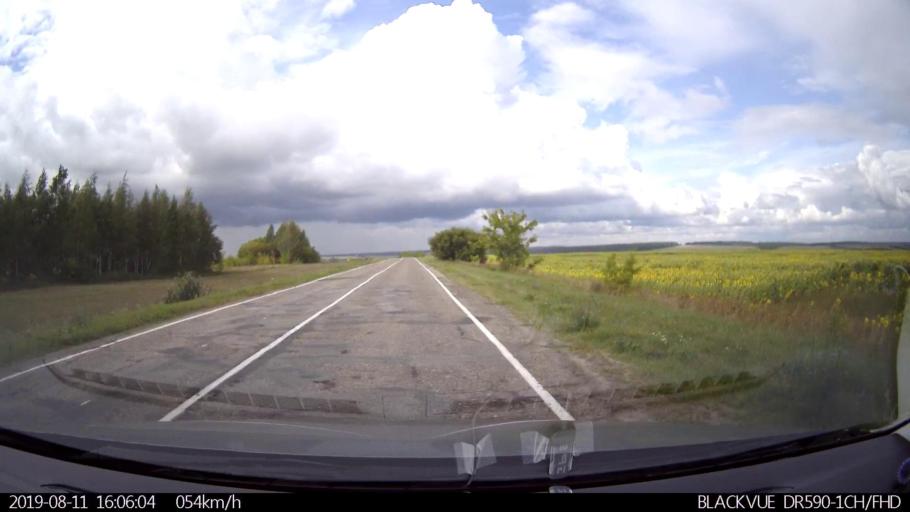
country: RU
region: Ulyanovsk
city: Ignatovka
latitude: 53.9657
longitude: 47.6492
